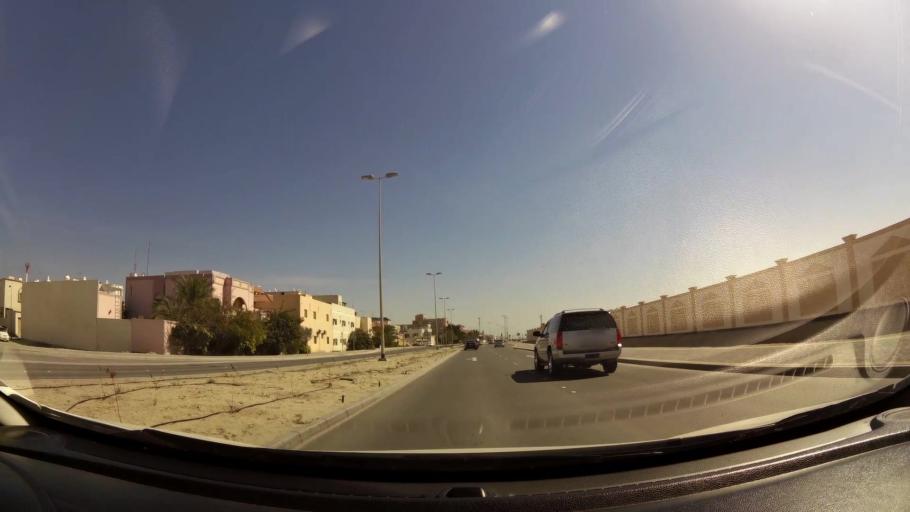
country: BH
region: Muharraq
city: Al Hadd
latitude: 26.2551
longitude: 50.6393
